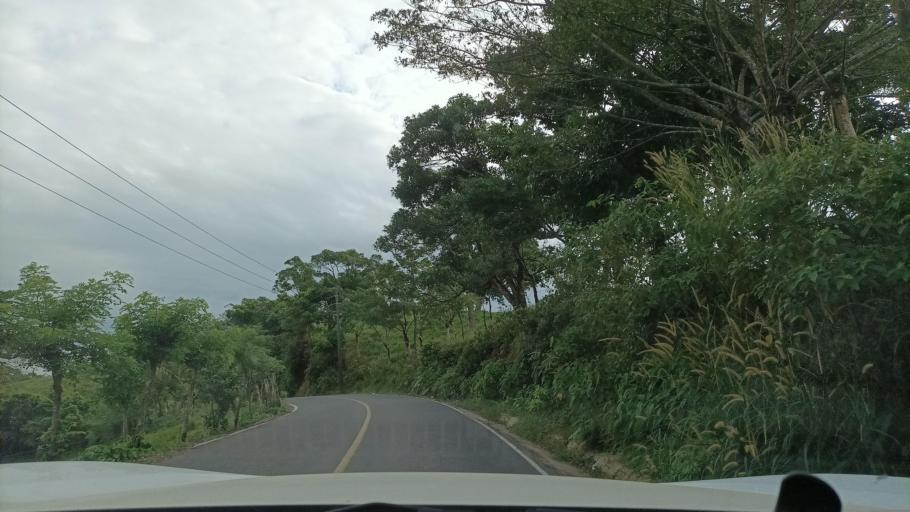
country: MX
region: Veracruz
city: Hidalgotitlan
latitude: 17.6893
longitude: -94.4615
